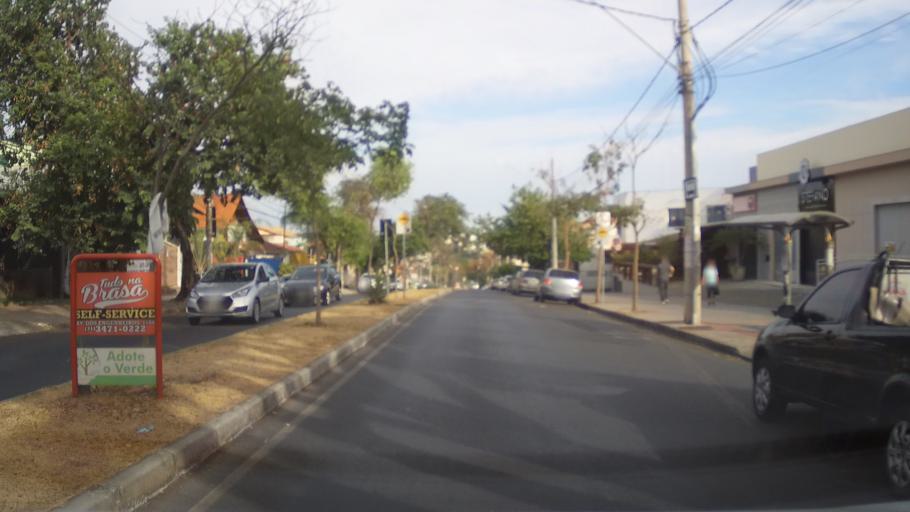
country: BR
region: Minas Gerais
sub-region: Contagem
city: Contagem
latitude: -19.8905
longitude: -44.0003
